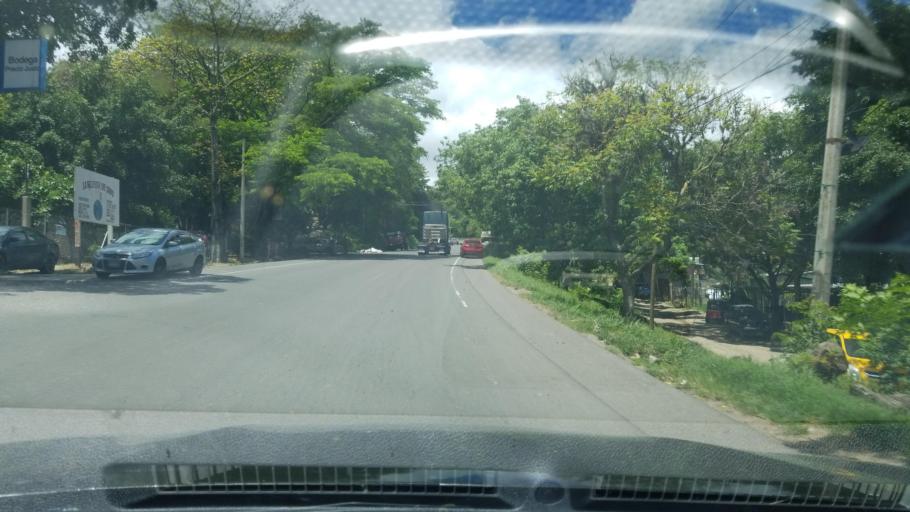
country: HN
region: Francisco Morazan
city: Rio Abajo
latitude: 14.1692
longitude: -87.2060
